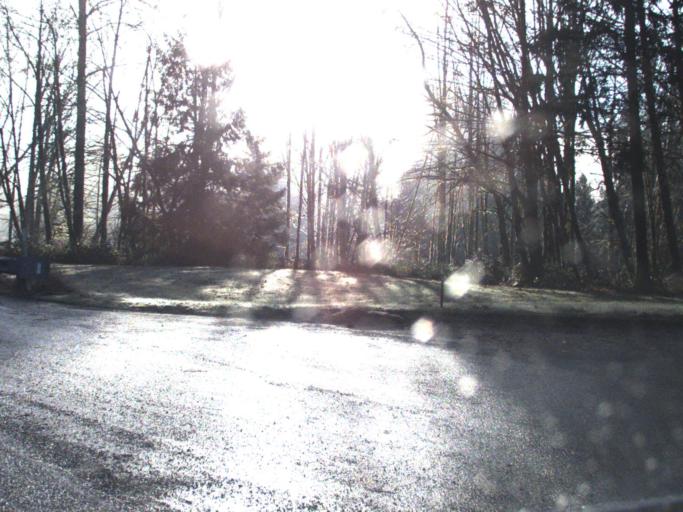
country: US
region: Washington
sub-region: Snohomish County
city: Darrington
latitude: 48.5351
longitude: -121.7344
